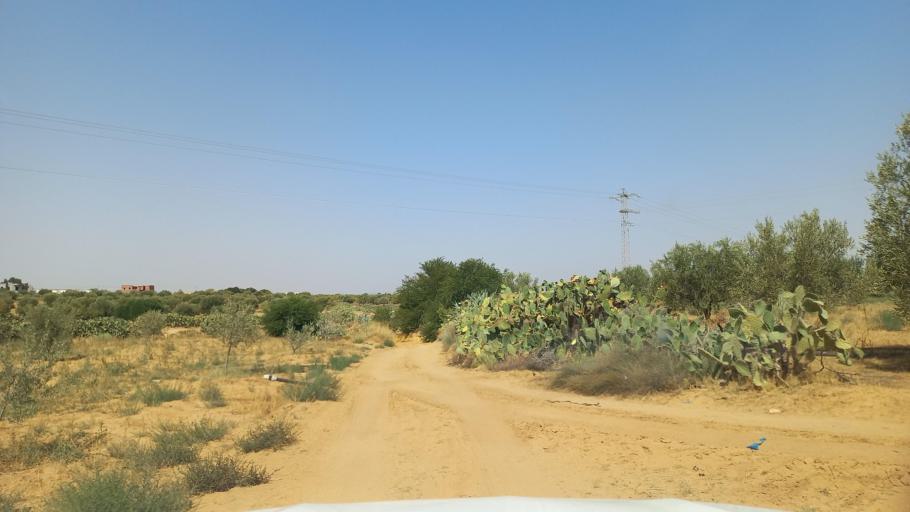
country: TN
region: Al Qasrayn
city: Kasserine
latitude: 35.2426
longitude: 9.0520
